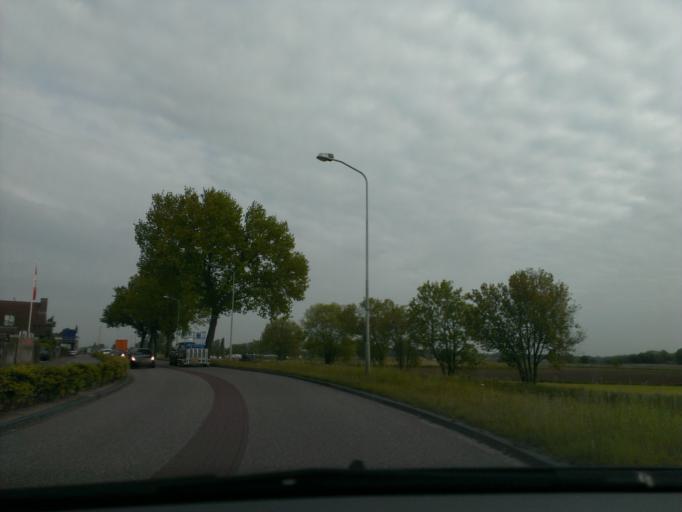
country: NL
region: Gelderland
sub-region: Gemeente Hattem
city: Hattem
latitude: 52.4746
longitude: 6.0721
